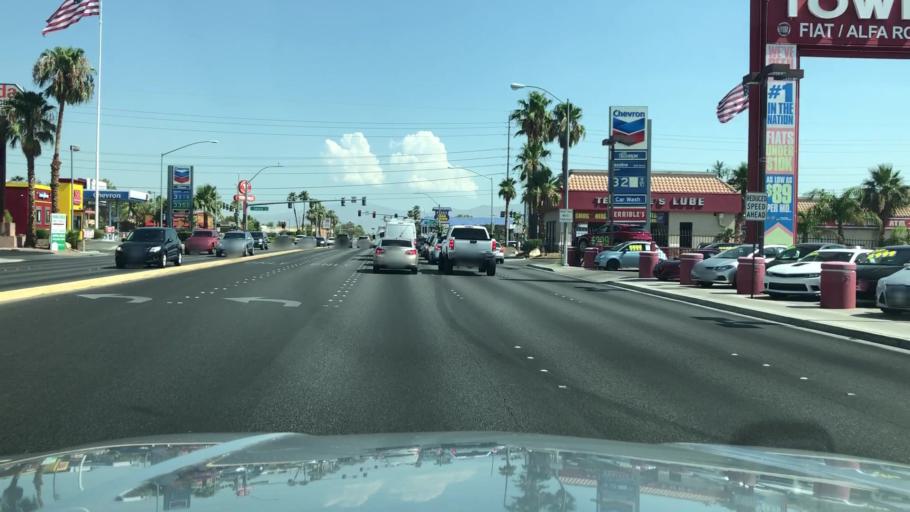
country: US
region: Nevada
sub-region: Clark County
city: Spring Valley
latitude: 36.1429
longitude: -115.2252
